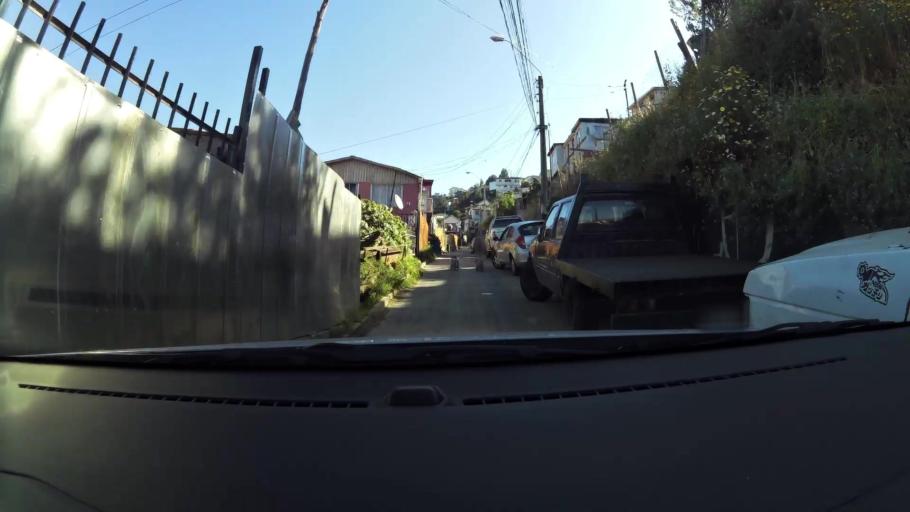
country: CL
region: Valparaiso
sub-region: Provincia de Valparaiso
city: Valparaiso
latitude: -33.0607
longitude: -71.6211
